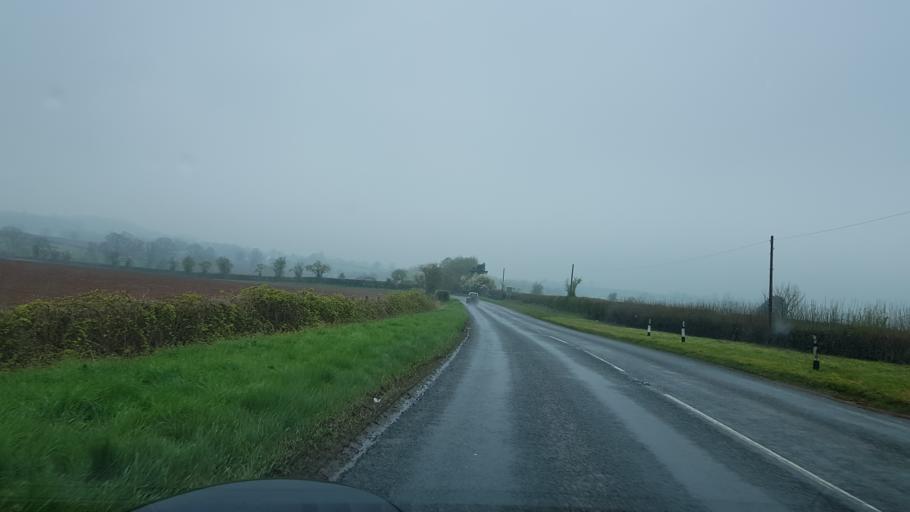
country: GB
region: England
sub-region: Herefordshire
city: Bromyard
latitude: 52.1720
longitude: -2.5294
